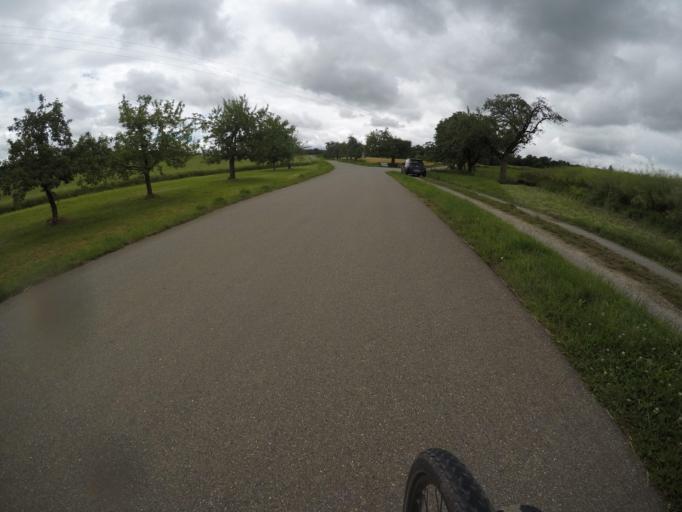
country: DE
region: Baden-Wuerttemberg
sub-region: Regierungsbezirk Stuttgart
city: Oberjettingen
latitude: 48.6051
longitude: 8.8126
